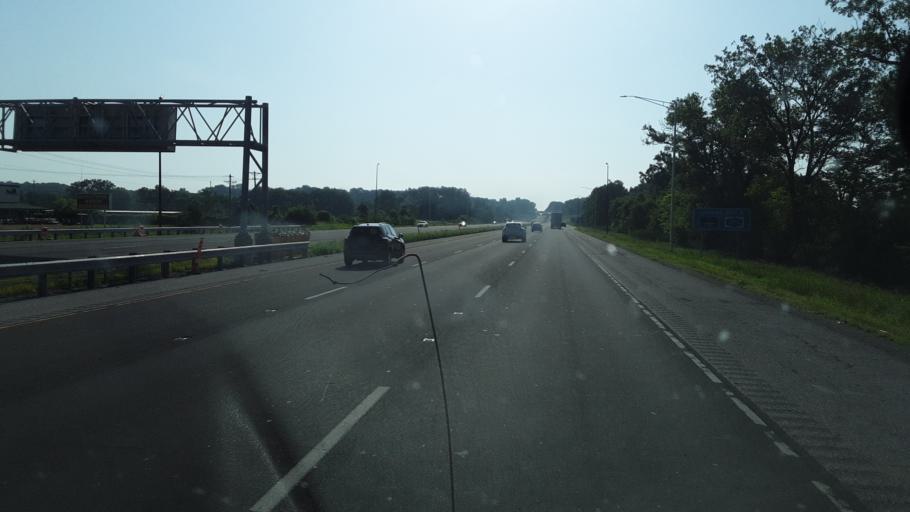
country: US
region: Illinois
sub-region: Madison County
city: Glen Carbon
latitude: 38.7567
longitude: -90.0233
